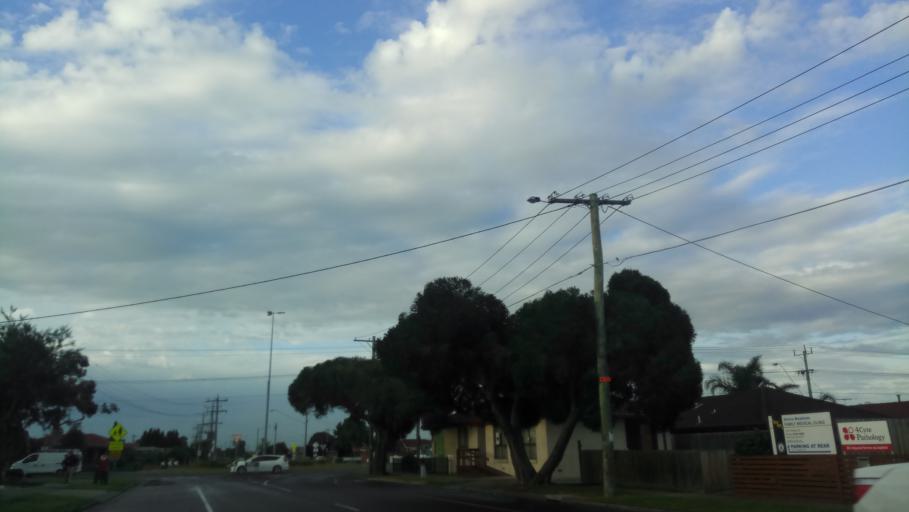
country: AU
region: Victoria
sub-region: Hobsons Bay
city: Altona Meadows
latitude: -37.8729
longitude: 144.7867
